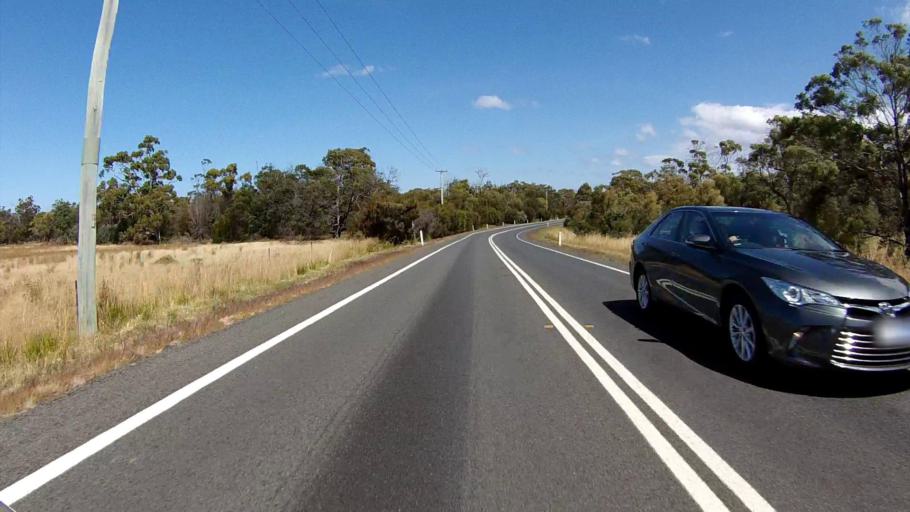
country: AU
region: Tasmania
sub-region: Break O'Day
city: St Helens
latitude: -42.0814
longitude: 148.0689
